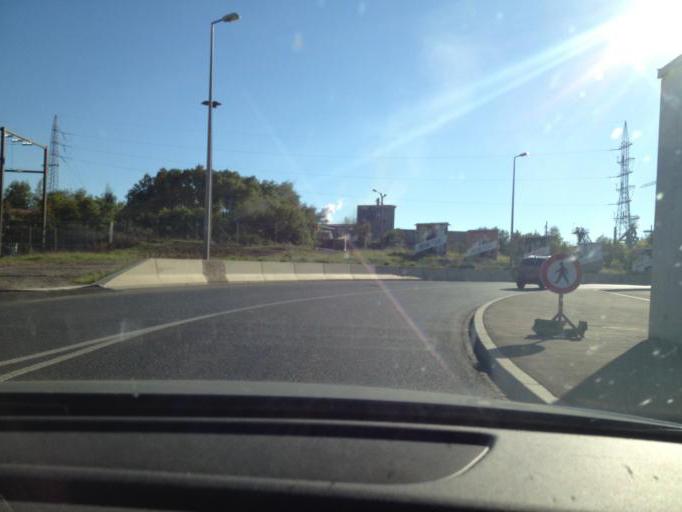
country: LU
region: Luxembourg
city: Soleuvre
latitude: 49.5072
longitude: 5.9559
